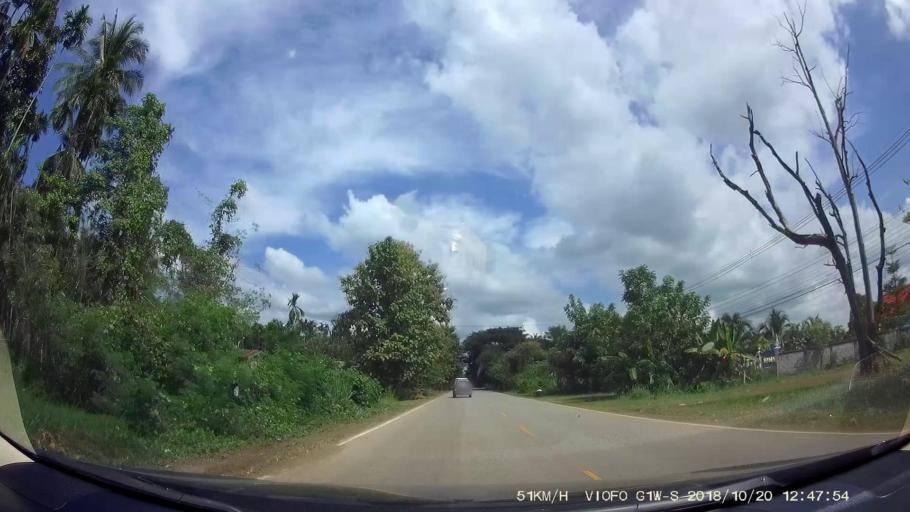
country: TH
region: Chaiyaphum
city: Khon San
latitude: 16.5349
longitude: 101.8887
